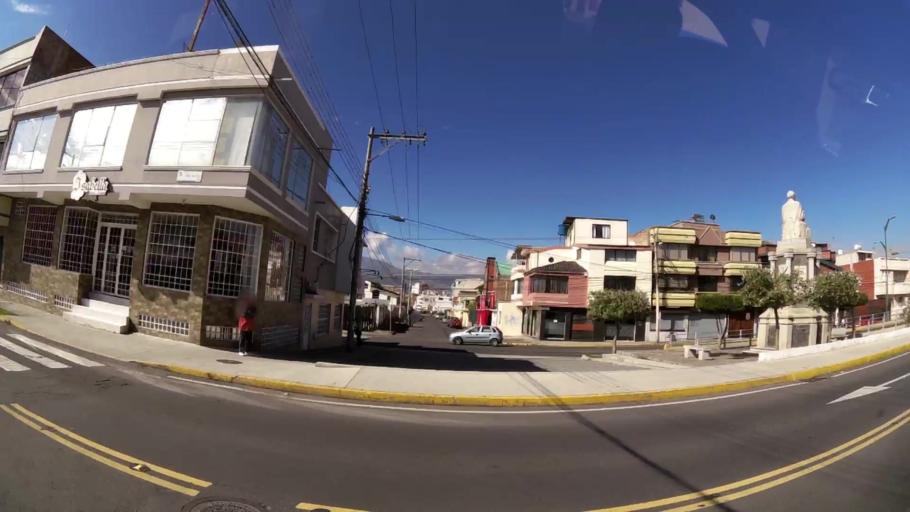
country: EC
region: Chimborazo
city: Riobamba
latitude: -1.6614
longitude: -78.6607
